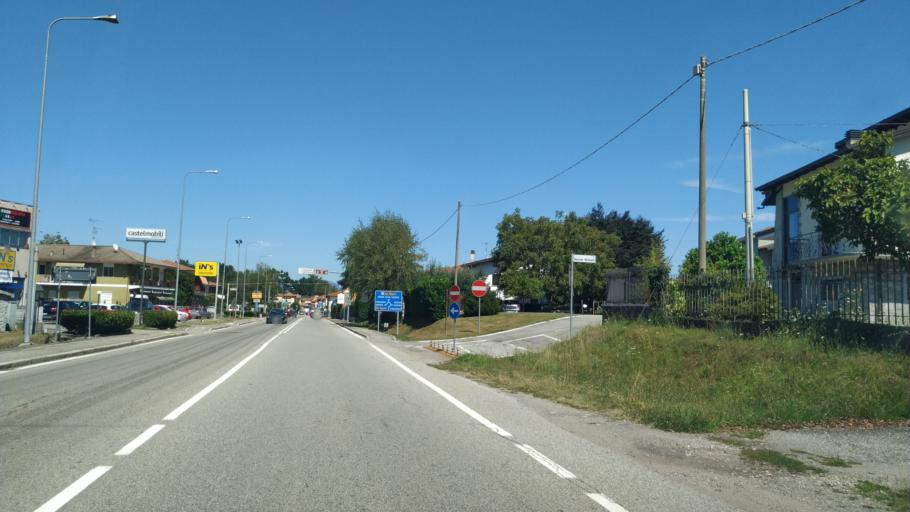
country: IT
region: Piedmont
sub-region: Provincia di Novara
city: Oleggio Castello
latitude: 45.7459
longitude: 8.5228
